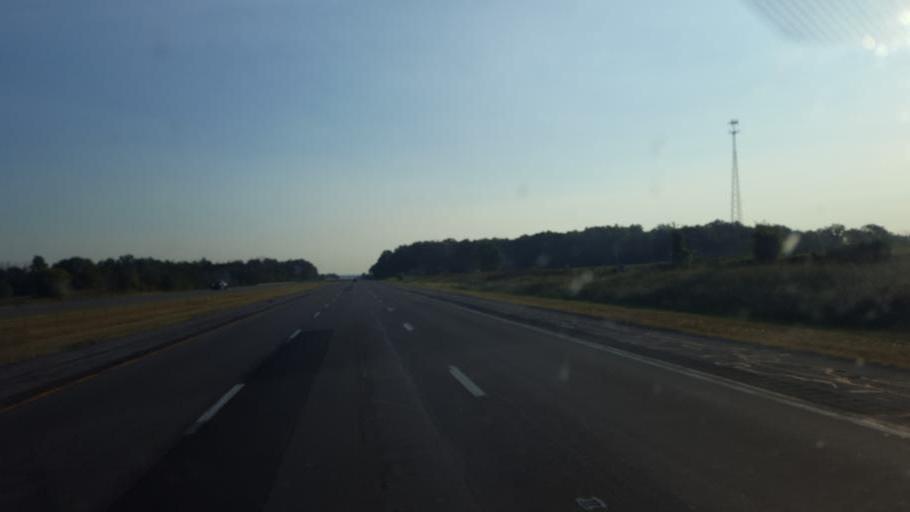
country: US
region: Ohio
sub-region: Wayne County
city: West Salem
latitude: 40.9556
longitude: -82.0677
